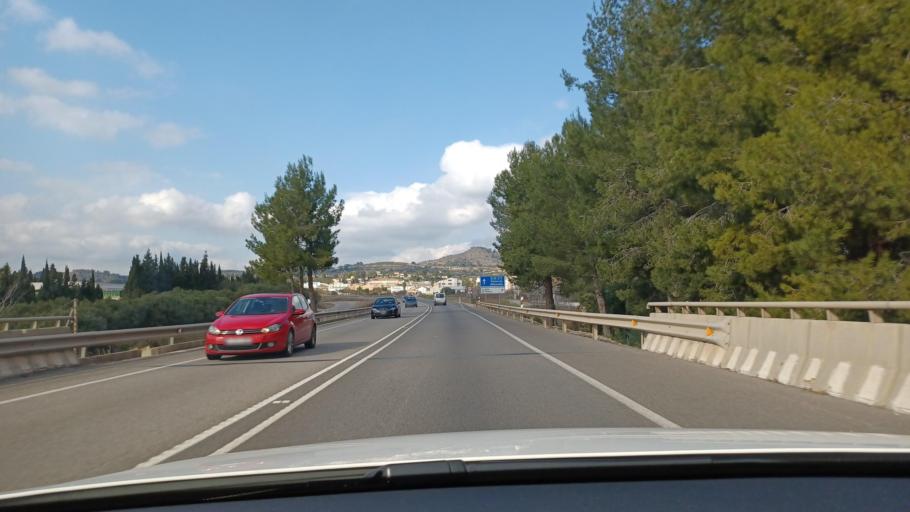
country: ES
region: Valencia
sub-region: Provincia de Valencia
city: Llosa de Ranes
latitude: 39.0102
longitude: -0.5329
